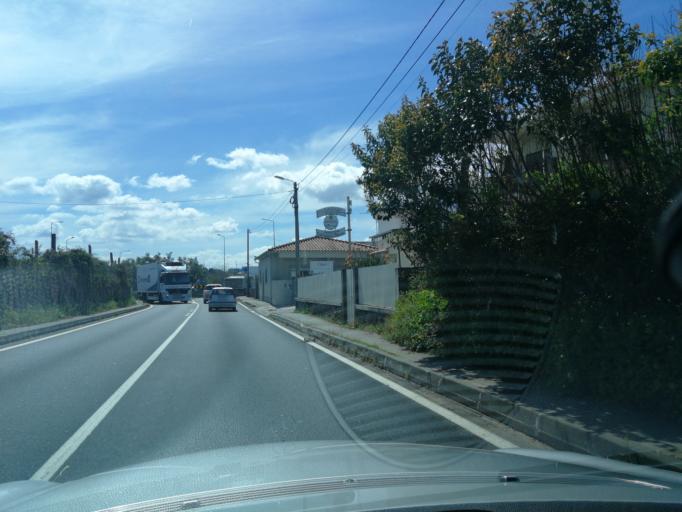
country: PT
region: Braga
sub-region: Vila Nova de Famalicao
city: Calendario
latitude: 41.4172
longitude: -8.5344
